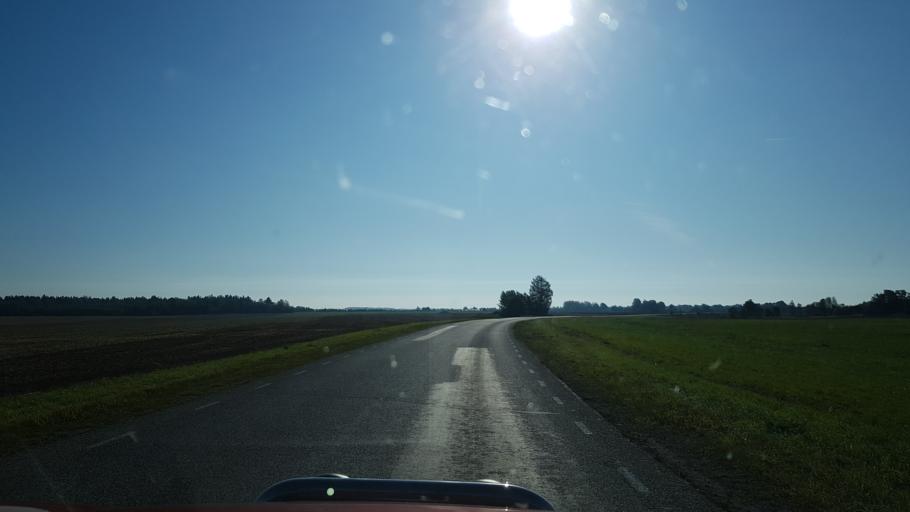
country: EE
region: Jogevamaa
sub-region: Tabivere vald
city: Tabivere
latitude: 58.6816
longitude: 26.6579
